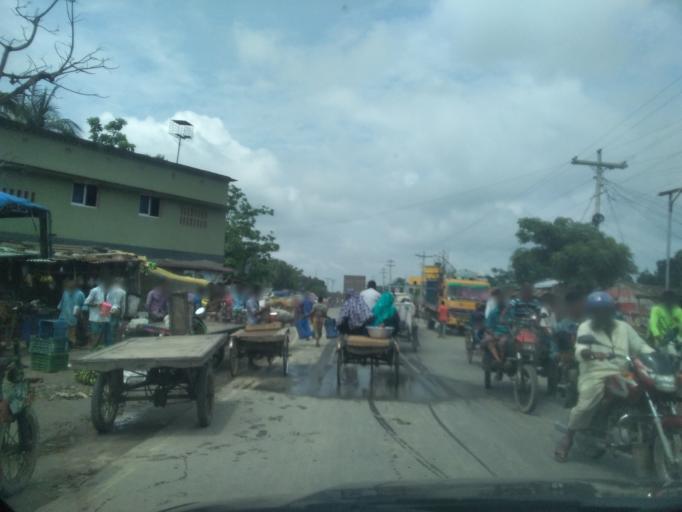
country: BD
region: Khulna
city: Kesabpur
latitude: 22.8238
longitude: 89.2728
